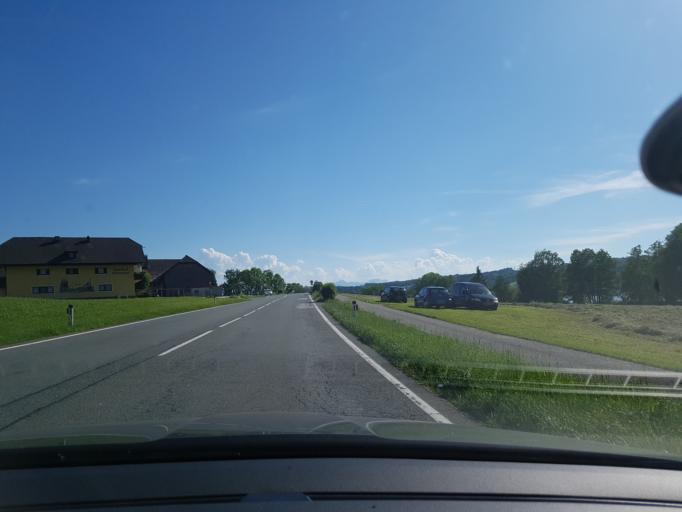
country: AT
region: Salzburg
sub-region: Politischer Bezirk Salzburg-Umgebung
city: Seeham
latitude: 47.9515
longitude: 13.0894
